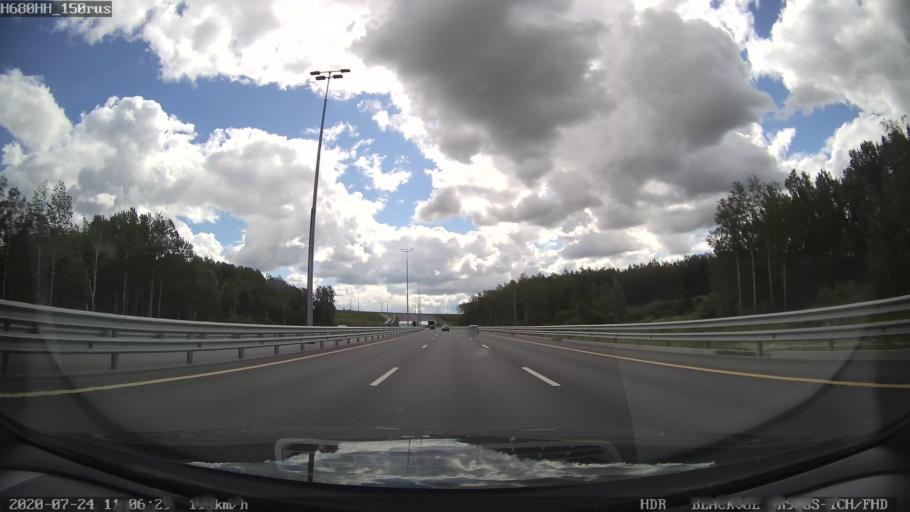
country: RU
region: St.-Petersburg
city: Shushary
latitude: 59.7621
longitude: 30.3772
